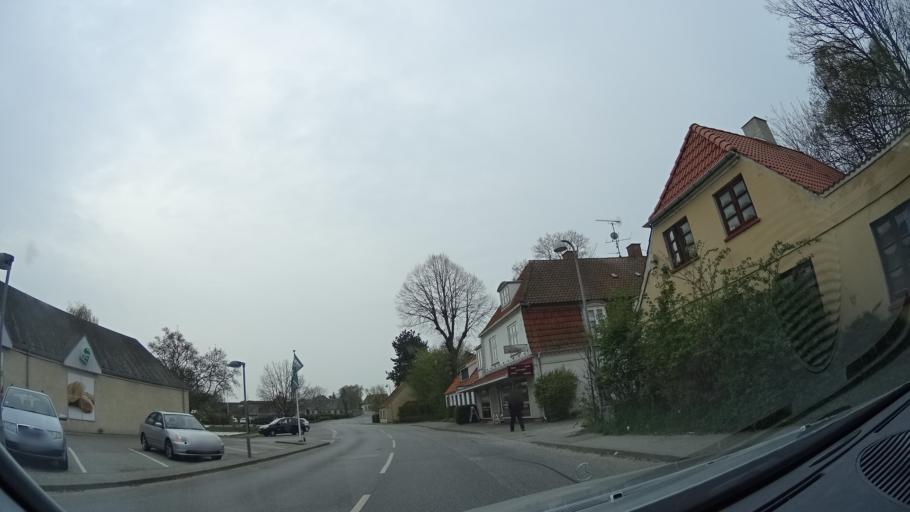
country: DK
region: Zealand
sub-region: Lejre Kommune
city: Ejby
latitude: 55.7081
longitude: 11.9004
